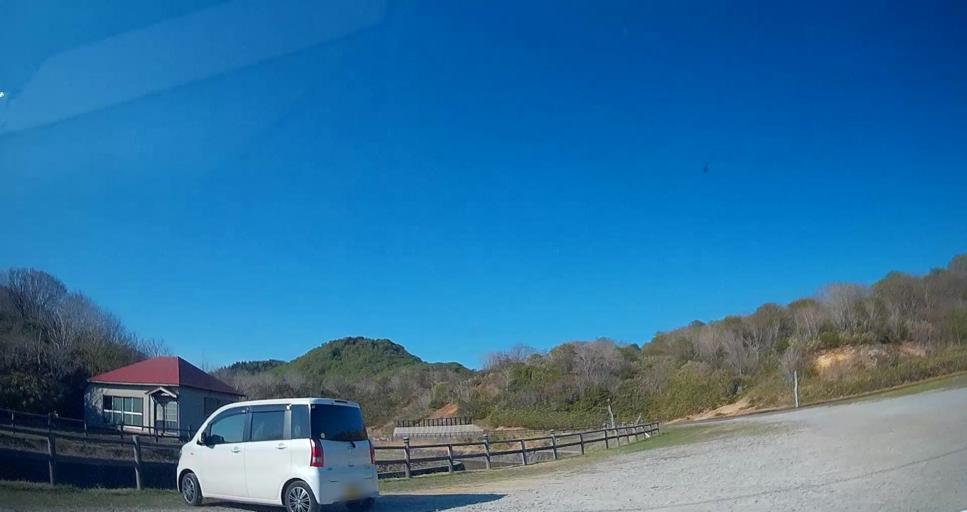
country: JP
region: Aomori
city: Mutsu
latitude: 41.3261
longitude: 141.0966
